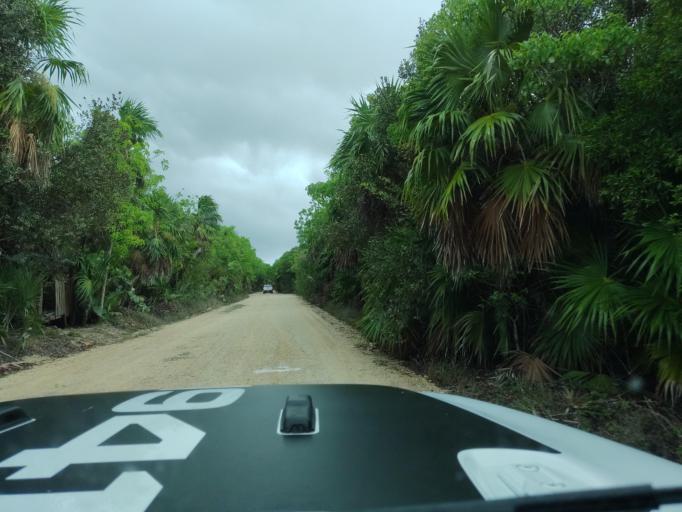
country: MX
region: Quintana Roo
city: Tulum
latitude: 20.0653
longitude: -87.4797
